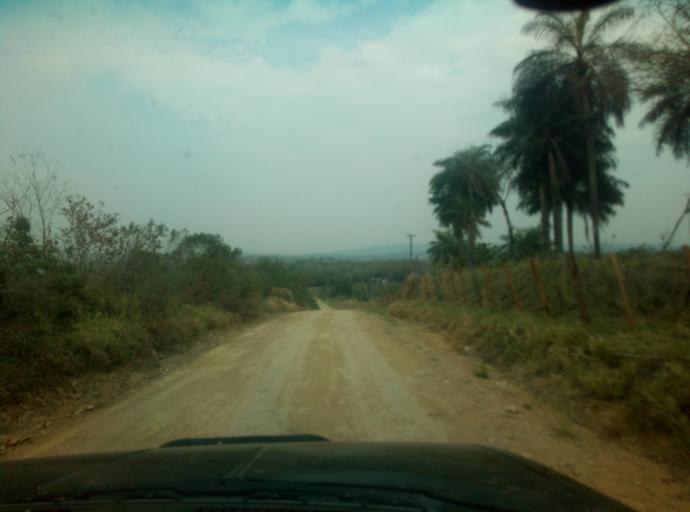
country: PY
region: Caaguazu
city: San Joaquin
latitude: -25.1030
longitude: -56.1312
